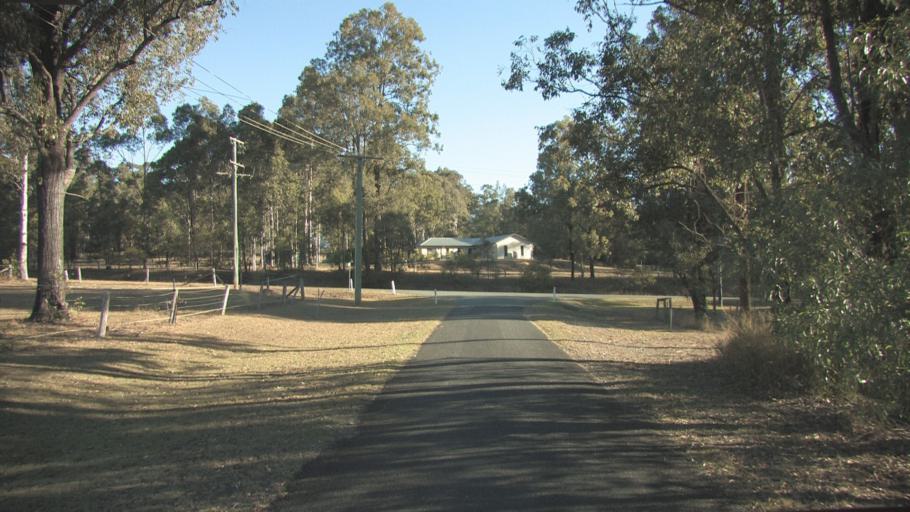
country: AU
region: Queensland
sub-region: Logan
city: Cedar Vale
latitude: -27.8504
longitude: 152.9939
